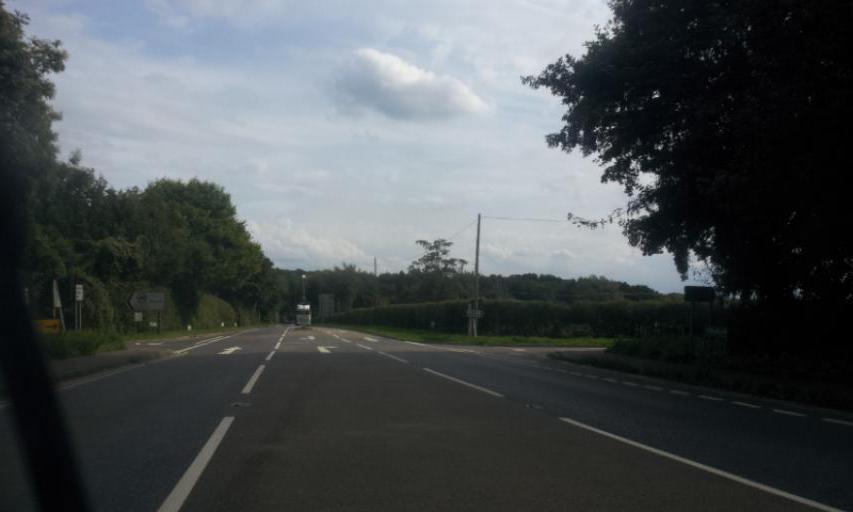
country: GB
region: England
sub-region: Kent
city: Kings Hill
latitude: 51.2566
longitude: 0.3691
